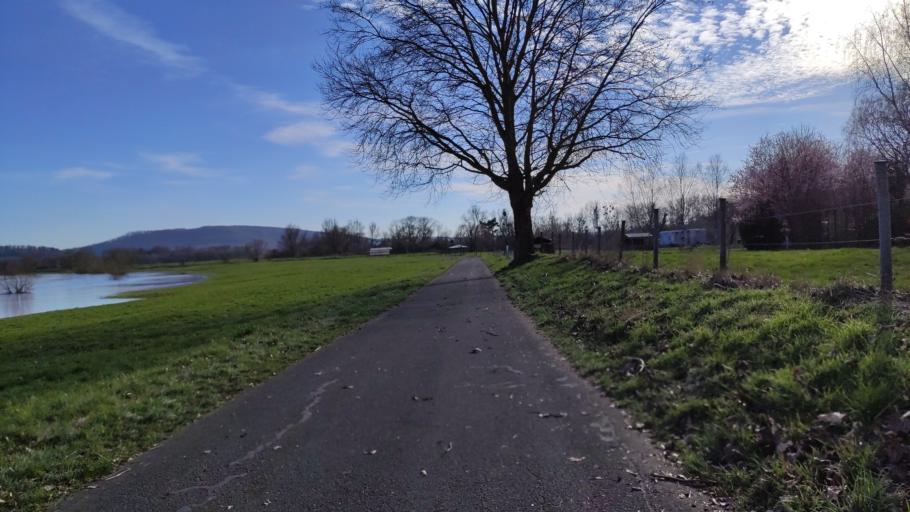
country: DE
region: Lower Saxony
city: Boffzen
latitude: 51.7451
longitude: 9.3750
